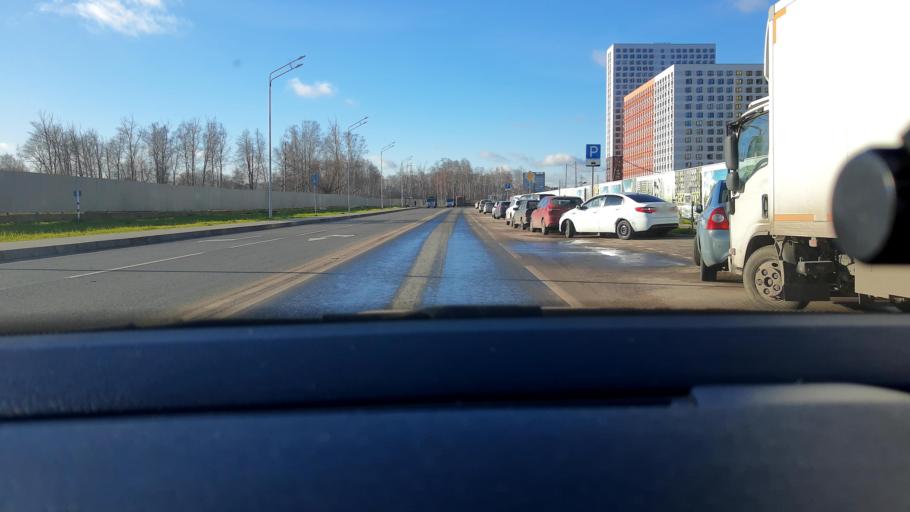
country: RU
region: Moskovskaya
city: Reutov
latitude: 55.7838
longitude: 37.8567
